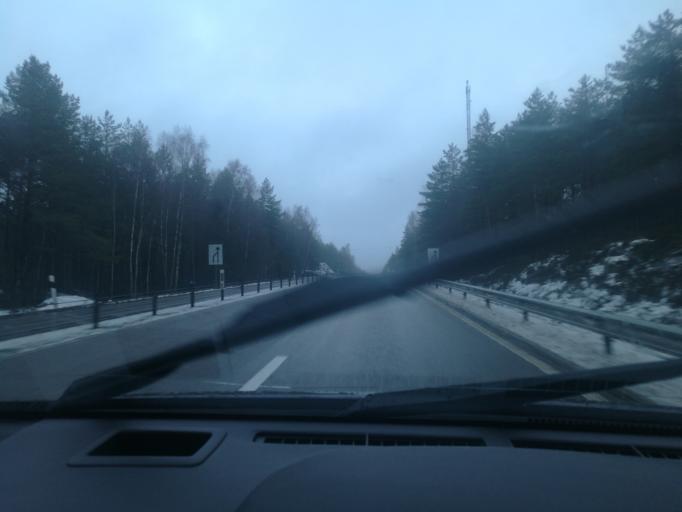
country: SE
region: OEstergoetland
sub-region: Norrkopings Kommun
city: Jursla
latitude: 58.7087
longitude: 16.1597
